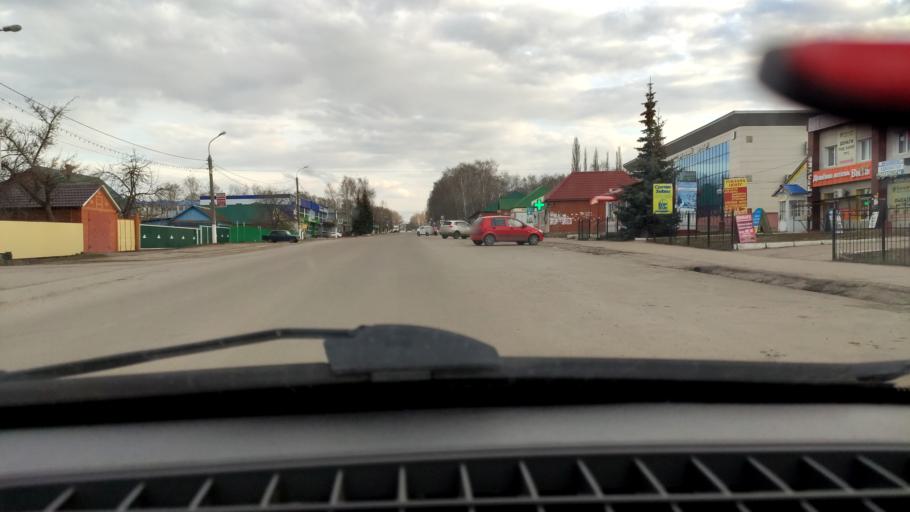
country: RU
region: Bashkortostan
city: Tolbazy
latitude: 54.0184
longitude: 55.8864
